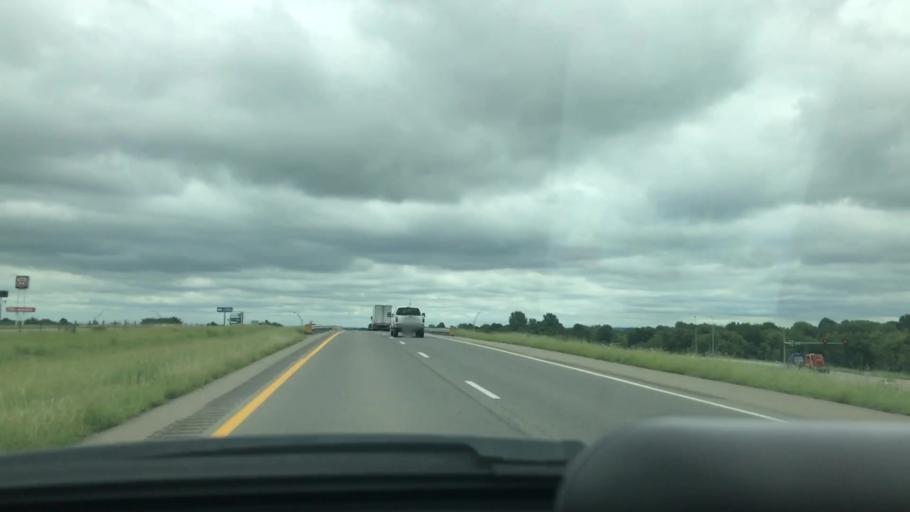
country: US
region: Oklahoma
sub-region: McIntosh County
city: Checotah
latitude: 35.4736
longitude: -95.5369
